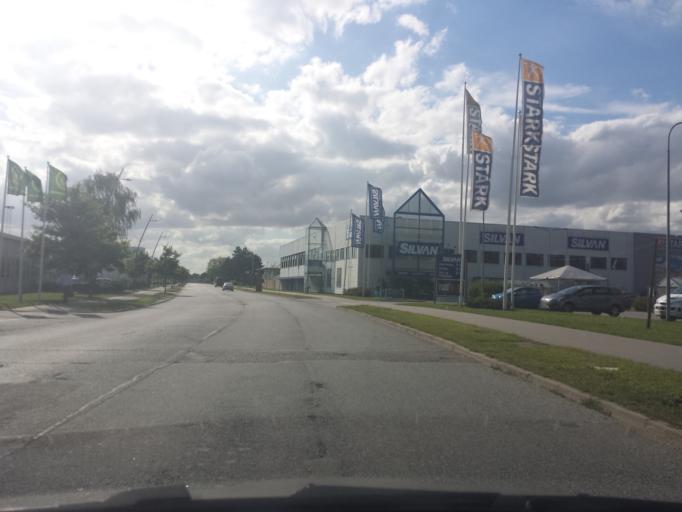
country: DK
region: Capital Region
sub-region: Glostrup Kommune
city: Glostrup
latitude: 55.6847
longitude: 12.3962
